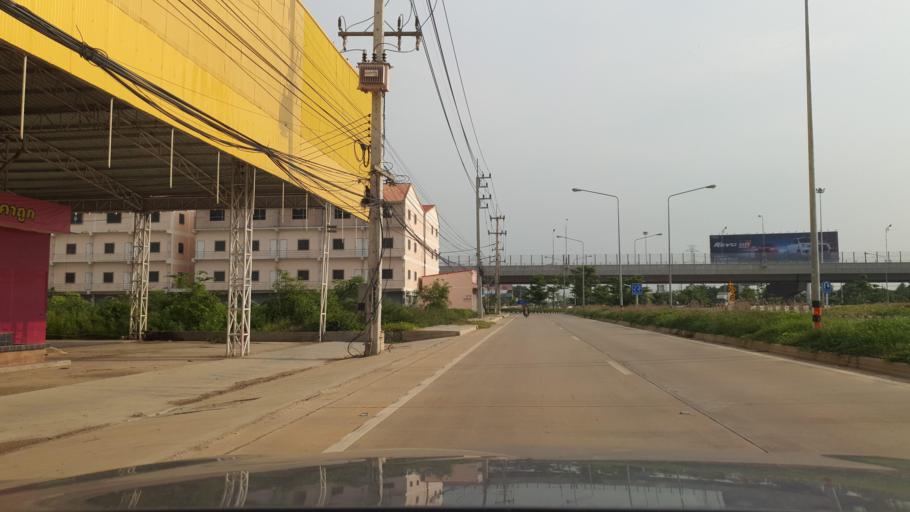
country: TH
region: Phitsanulok
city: Phitsanulok
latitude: 16.8164
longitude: 100.3306
